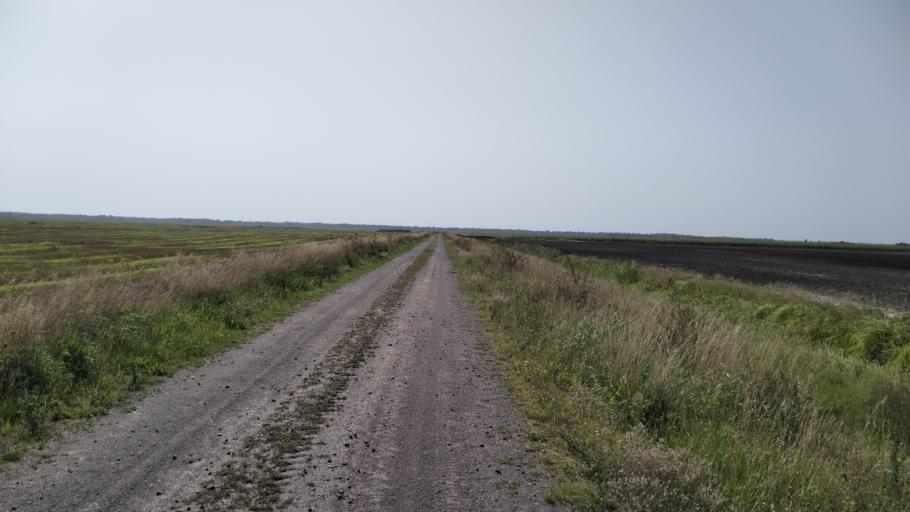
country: BY
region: Brest
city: Davyd-Haradok
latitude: 51.9954
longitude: 27.1648
